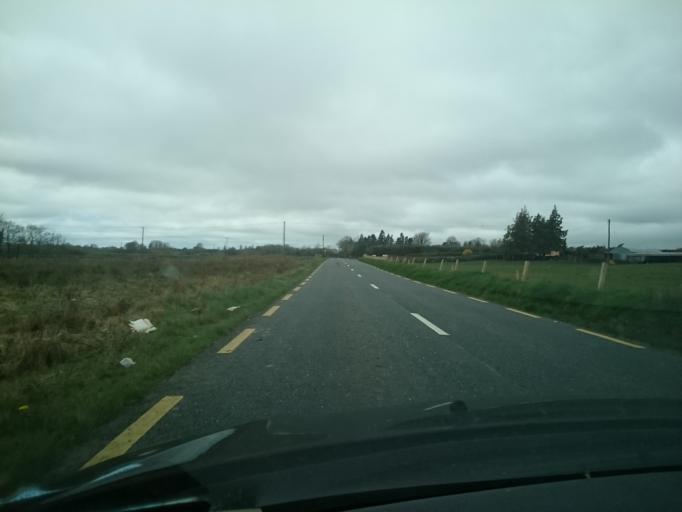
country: IE
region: Connaught
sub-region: Maigh Eo
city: Ballyhaunis
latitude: 53.7411
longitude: -8.8358
